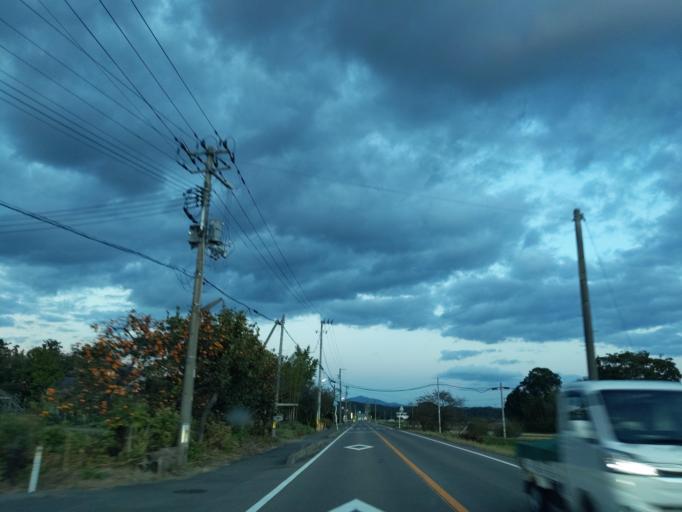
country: JP
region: Fukushima
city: Motomiya
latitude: 37.4889
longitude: 140.3849
